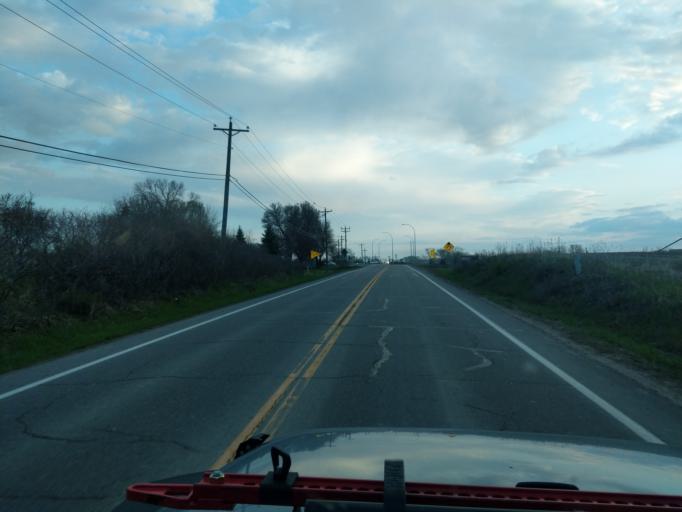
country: US
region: Minnesota
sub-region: Hennepin County
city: Rogers
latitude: 45.1605
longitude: -93.5216
